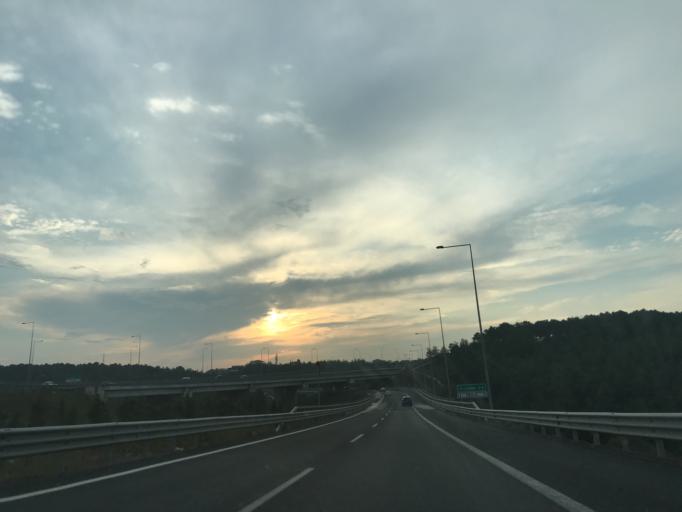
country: TR
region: Istanbul
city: Umraniye
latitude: 41.0498
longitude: 29.1297
